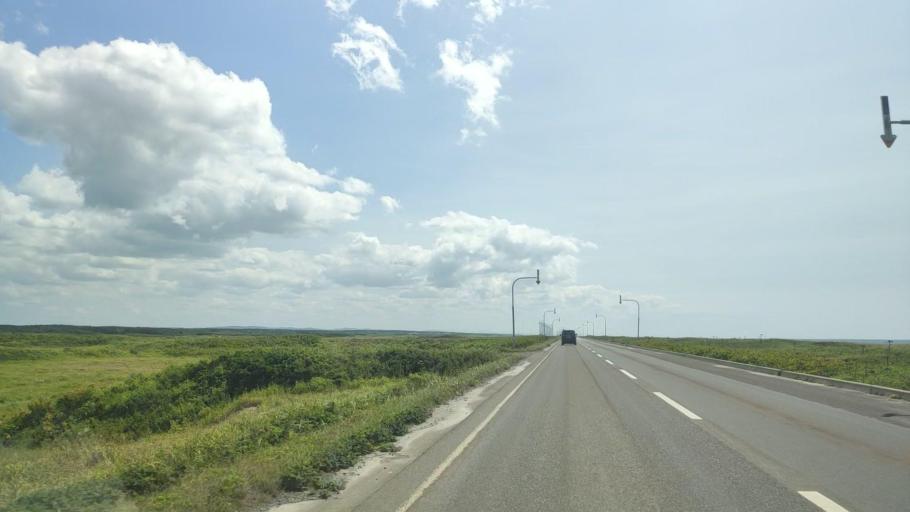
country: JP
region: Hokkaido
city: Makubetsu
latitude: 45.0154
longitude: 141.6742
